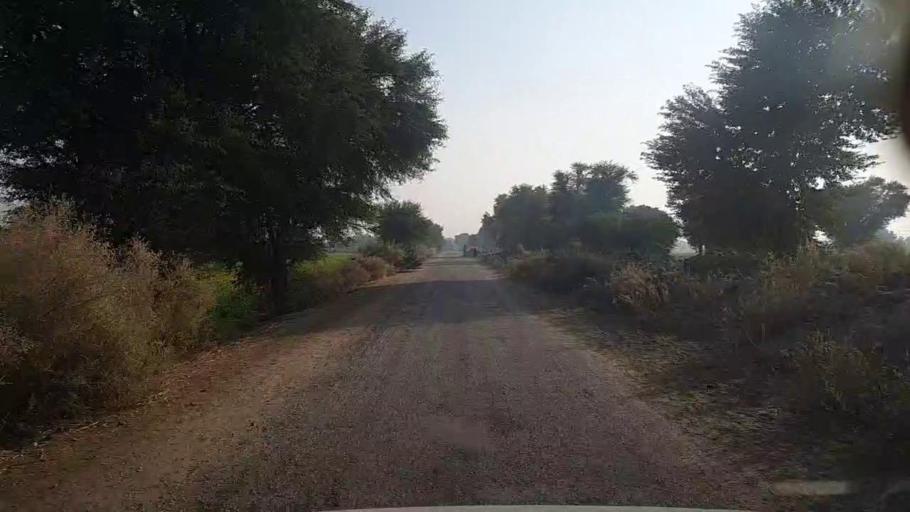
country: PK
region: Sindh
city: Karaundi
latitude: 26.7552
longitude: 68.4766
